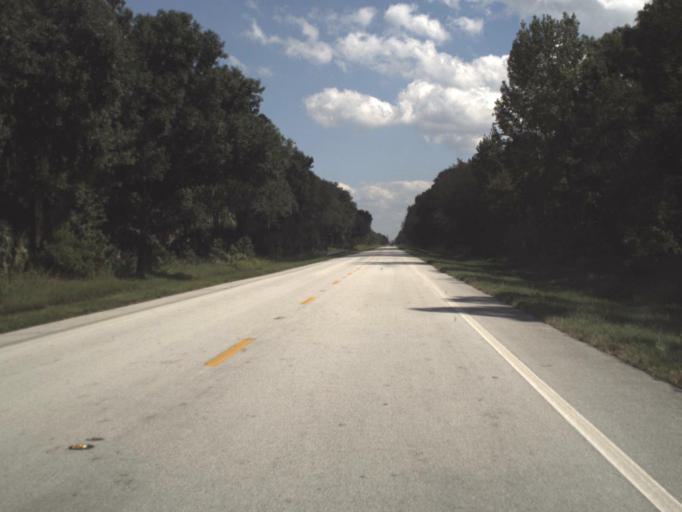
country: US
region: Florida
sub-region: Highlands County
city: Sebring
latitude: 27.4123
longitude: -81.5460
